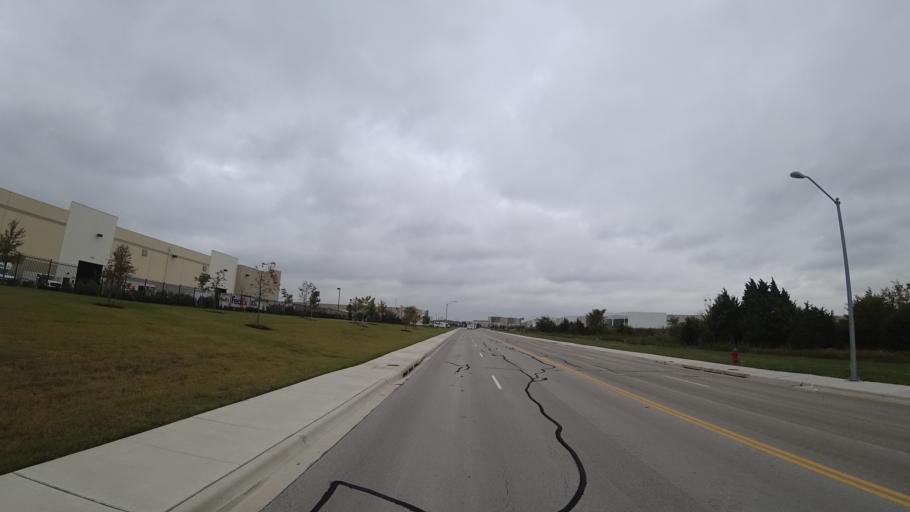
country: US
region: Texas
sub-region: Travis County
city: Pflugerville
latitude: 30.4174
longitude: -97.5904
